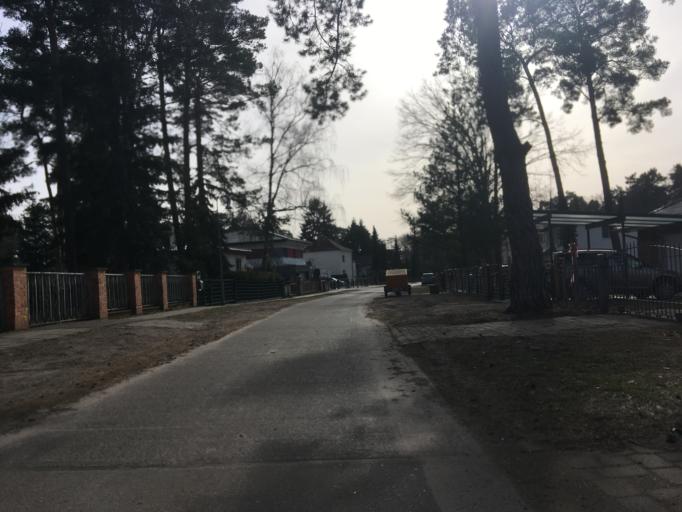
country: DE
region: Berlin
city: Schmockwitz
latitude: 52.3918
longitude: 13.6302
